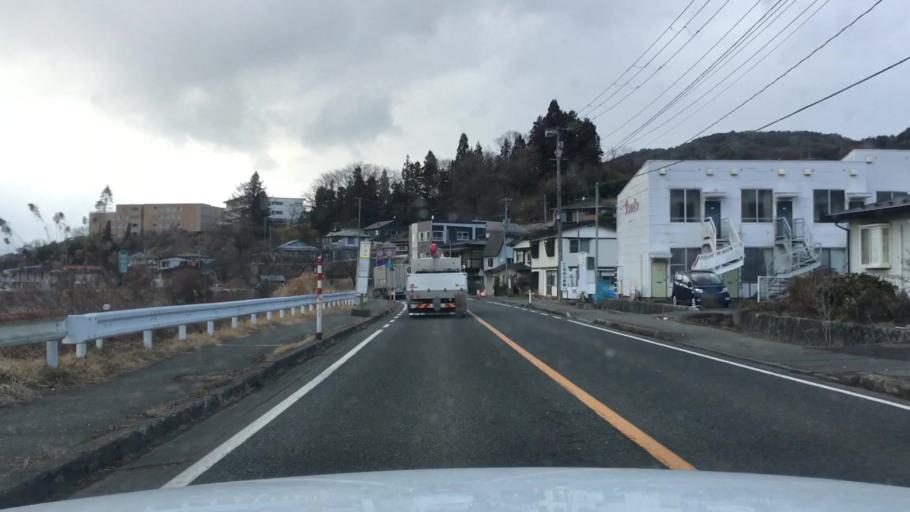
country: JP
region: Iwate
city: Morioka-shi
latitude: 39.6856
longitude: 141.1819
